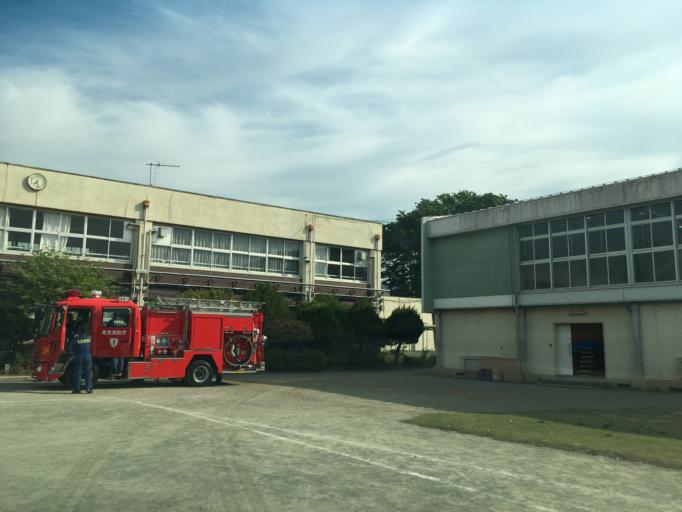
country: JP
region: Tokyo
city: Tanashicho
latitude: 35.7850
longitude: 139.5258
